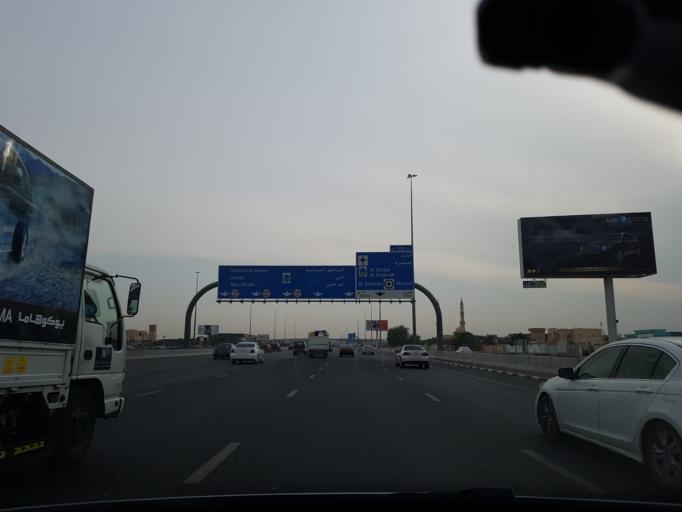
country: AE
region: Ash Shariqah
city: Sharjah
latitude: 25.3467
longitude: 55.4739
